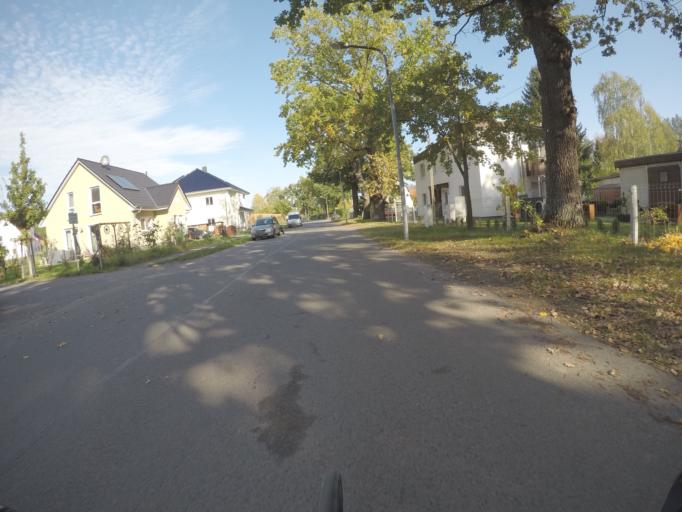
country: DE
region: Brandenburg
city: Oranienburg
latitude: 52.7421
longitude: 13.2248
